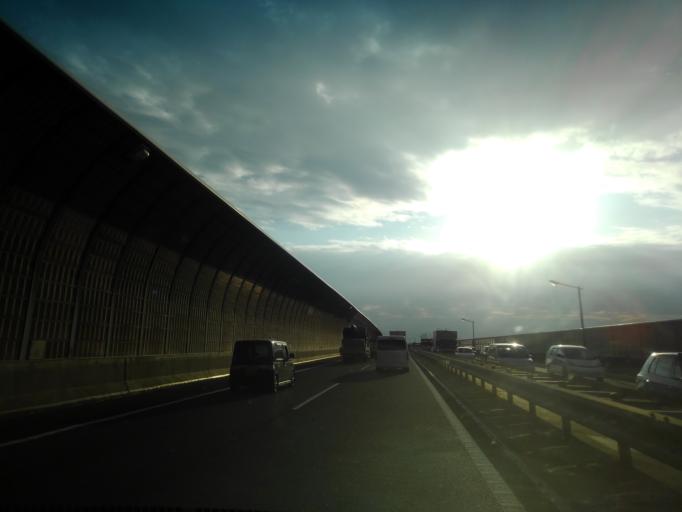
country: JP
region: Saitama
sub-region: Kawaguchi-shi
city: Hatogaya-honcho
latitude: 35.8497
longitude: 139.7622
